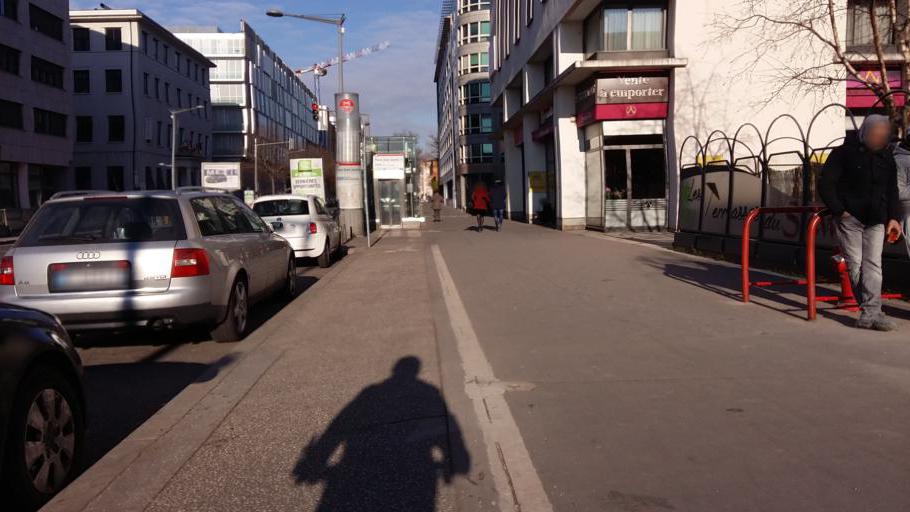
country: FR
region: Rhone-Alpes
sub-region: Departement du Rhone
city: Lyon
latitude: 45.7376
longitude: 4.8374
